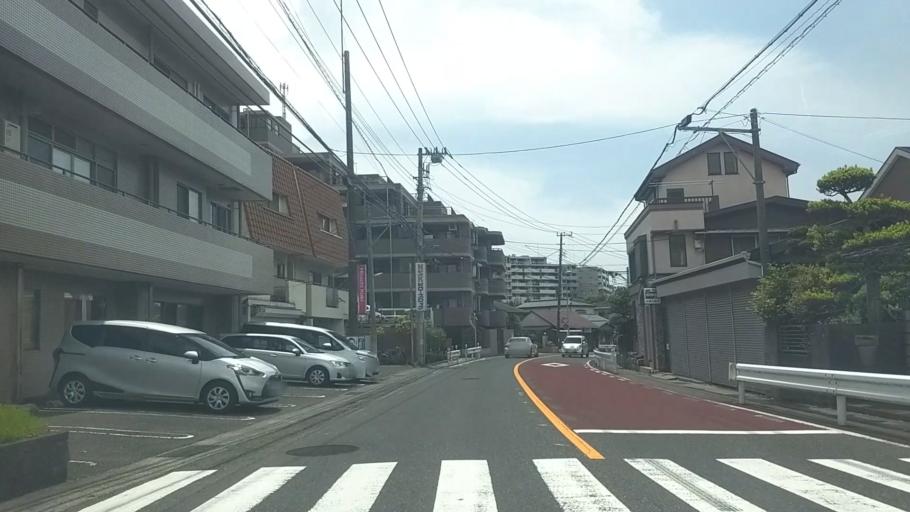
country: JP
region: Kanagawa
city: Fujisawa
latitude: 35.3466
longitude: 139.4922
